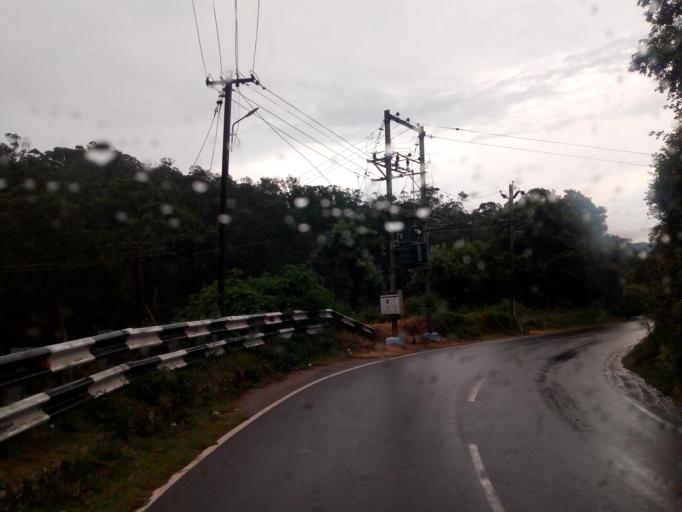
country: IN
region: Tamil Nadu
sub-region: Nilgiri
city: Wellington
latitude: 11.3438
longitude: 76.8026
